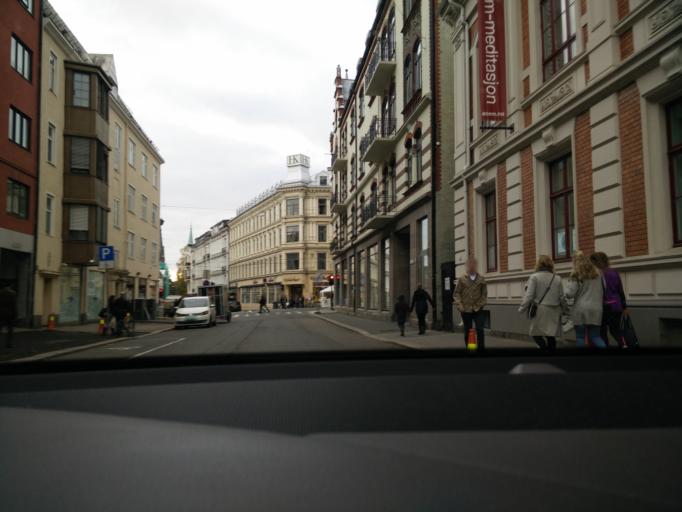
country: NO
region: Oslo
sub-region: Oslo
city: Oslo
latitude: 59.9251
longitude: 10.7252
